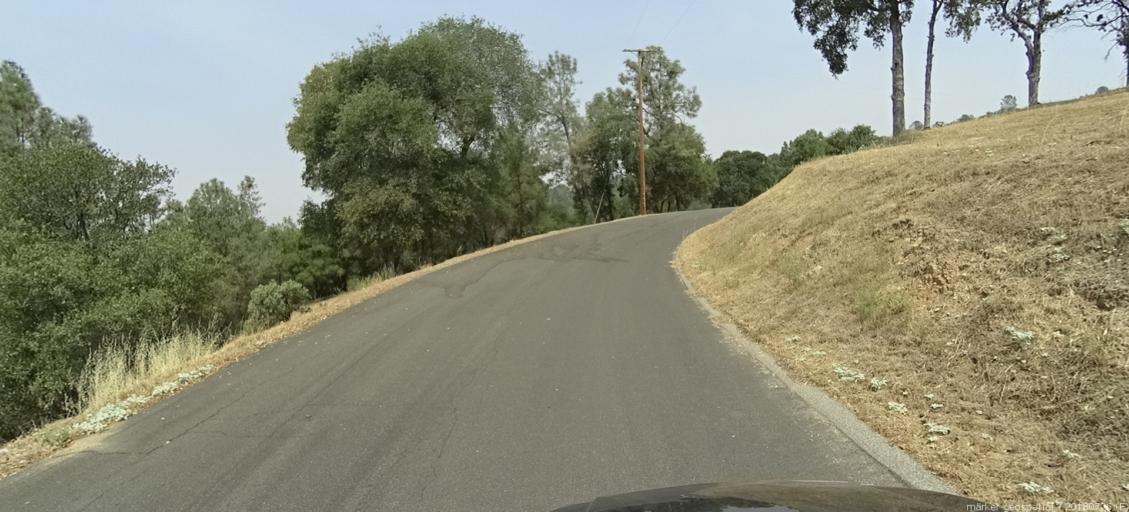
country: US
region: California
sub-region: Madera County
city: Coarsegold
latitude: 37.2456
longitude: -119.6932
